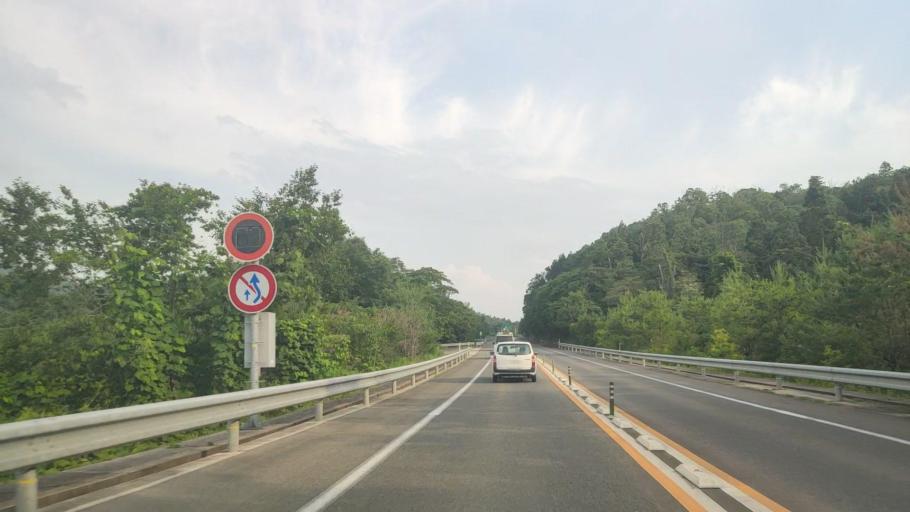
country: JP
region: Tottori
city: Kurayoshi
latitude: 35.4595
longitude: 133.8099
